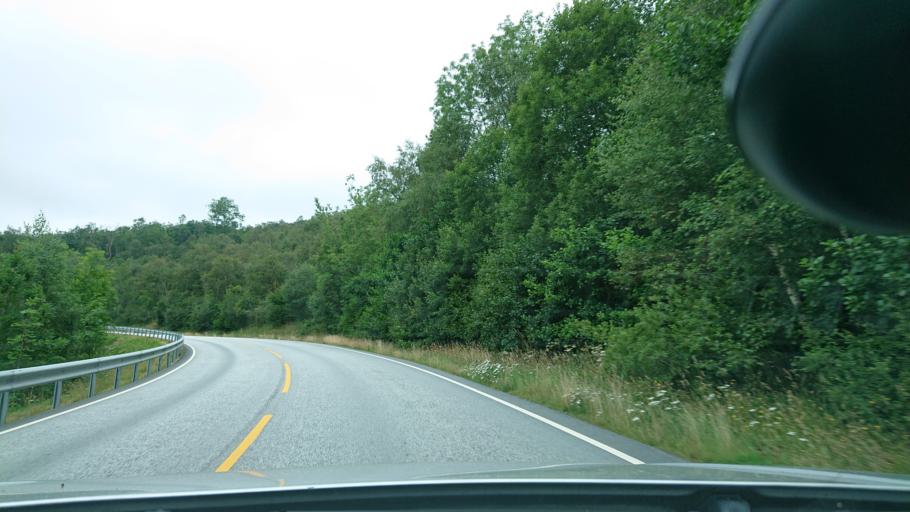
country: NO
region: Rogaland
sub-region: Hjelmeland
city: Hjelmelandsvagen
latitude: 59.1719
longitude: 6.1609
